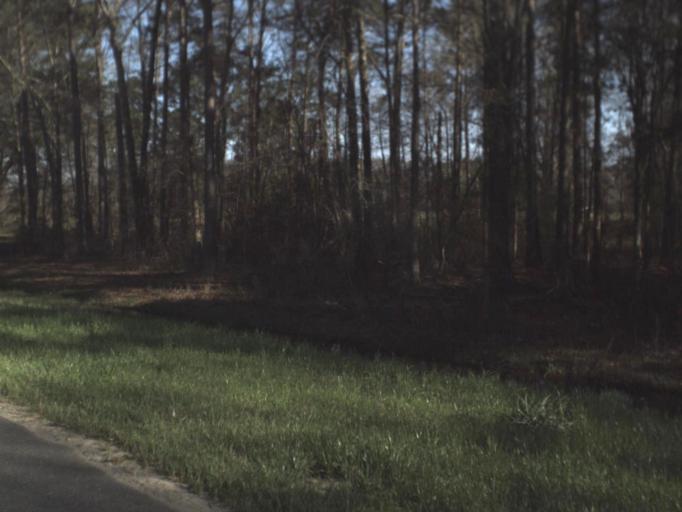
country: US
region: Florida
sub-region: Washington County
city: Chipley
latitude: 30.7878
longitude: -85.4310
